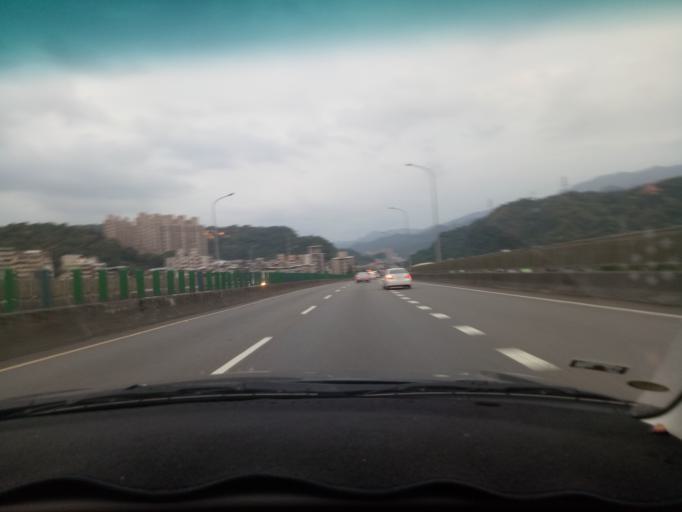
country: TW
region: Taiwan
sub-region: Keelung
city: Keelung
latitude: 25.1046
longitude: 121.7356
